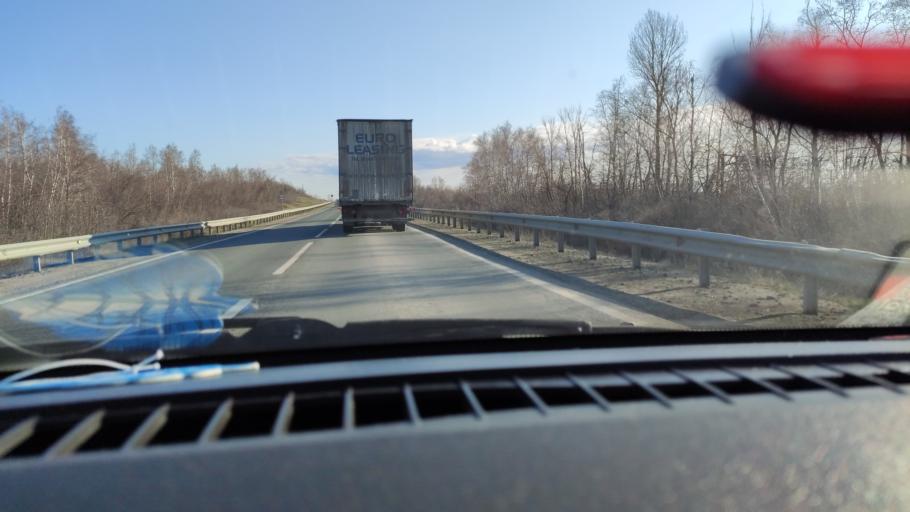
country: RU
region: Saratov
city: Dukhovnitskoye
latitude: 52.6772
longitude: 48.2287
